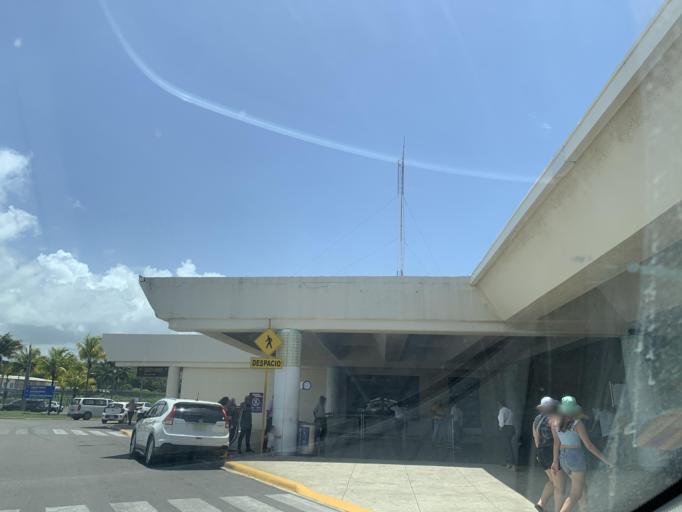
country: DO
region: Puerto Plata
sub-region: Puerto Plata
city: Puerto Plata
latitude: 19.7550
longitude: -70.5634
